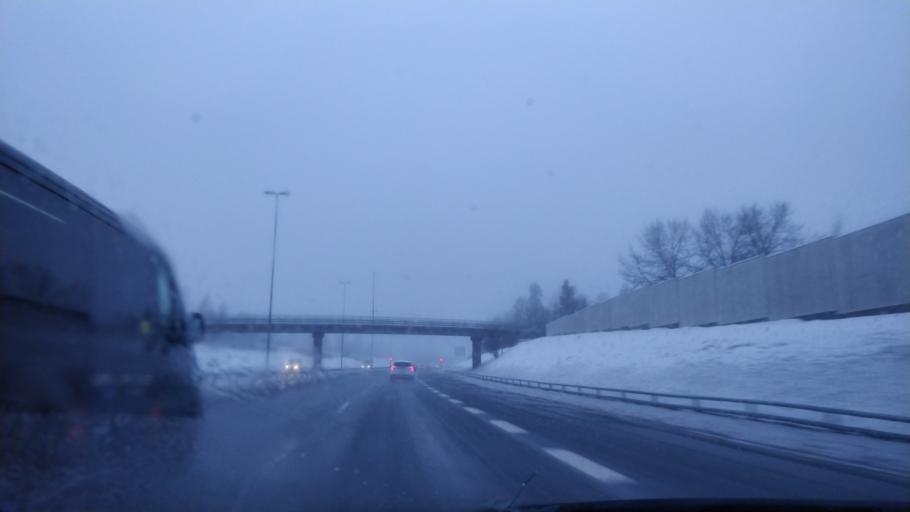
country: FI
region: Lapland
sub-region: Kemi-Tornio
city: Kemi
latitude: 65.7461
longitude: 24.5803
